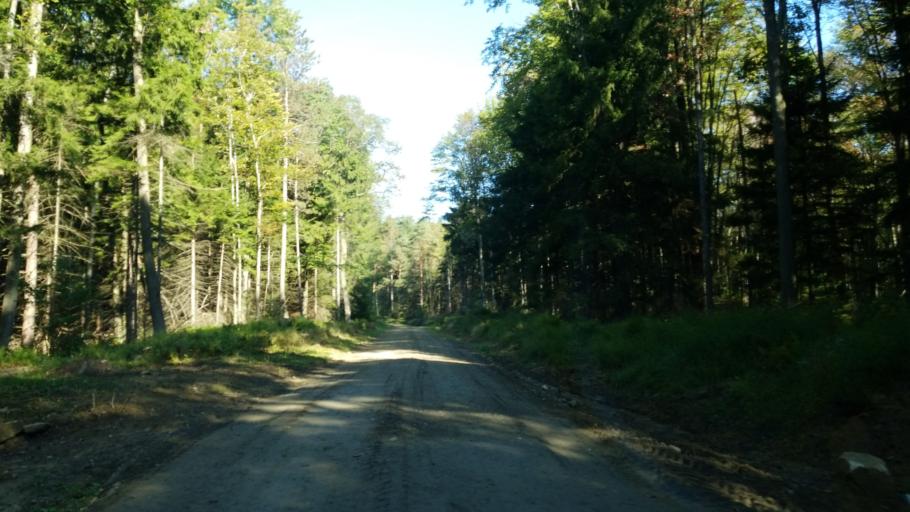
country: US
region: Pennsylvania
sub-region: Clearfield County
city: Treasure Lake
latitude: 41.1298
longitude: -78.5654
